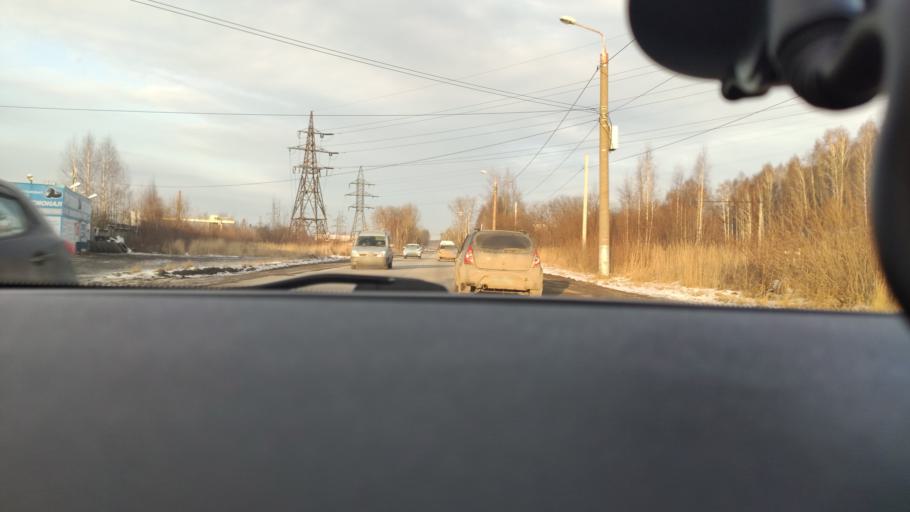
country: RU
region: Perm
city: Perm
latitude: 58.1013
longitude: 56.3589
